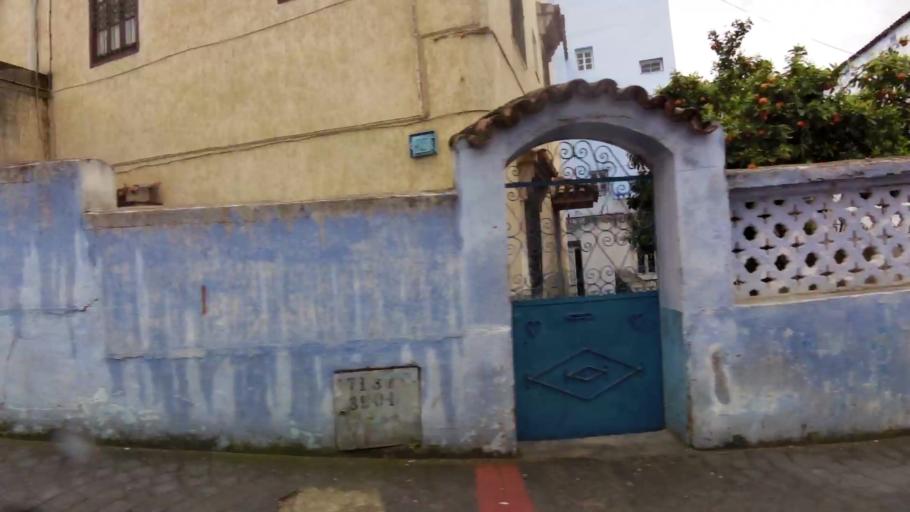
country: MA
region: Tanger-Tetouan
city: Chefchaouene
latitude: 35.1673
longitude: -5.2690
